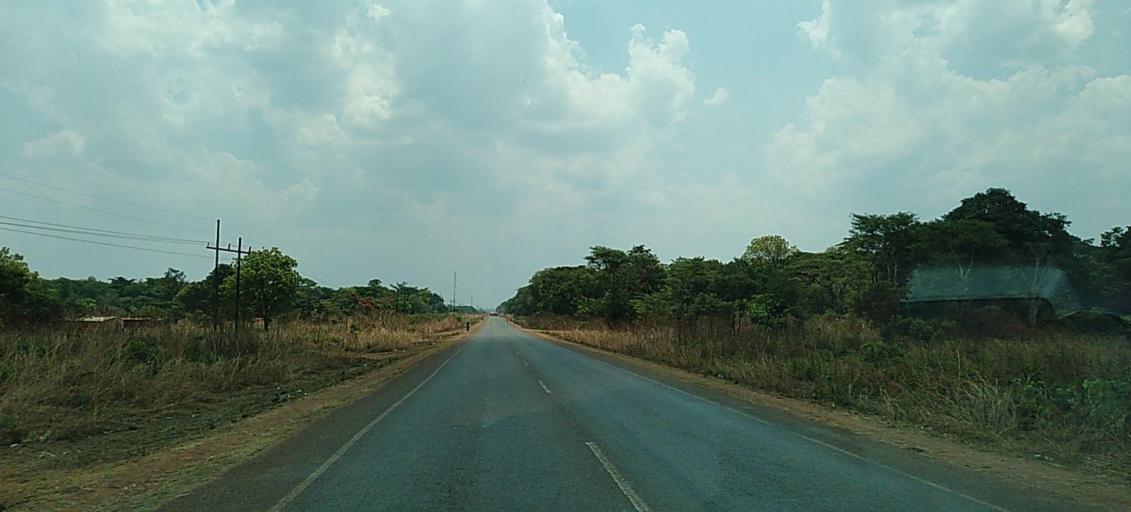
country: ZM
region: Copperbelt
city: Kalulushi
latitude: -12.8415
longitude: 28.0019
